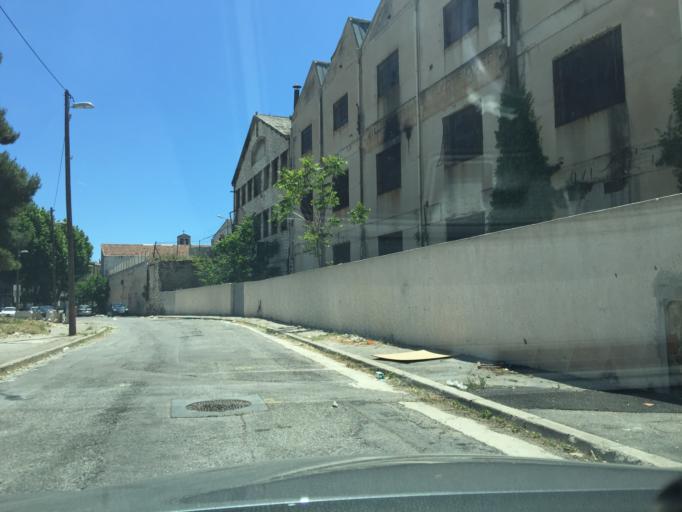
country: FR
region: Provence-Alpes-Cote d'Azur
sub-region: Departement des Bouches-du-Rhone
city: Marseille 14
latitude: 43.3262
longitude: 5.3675
